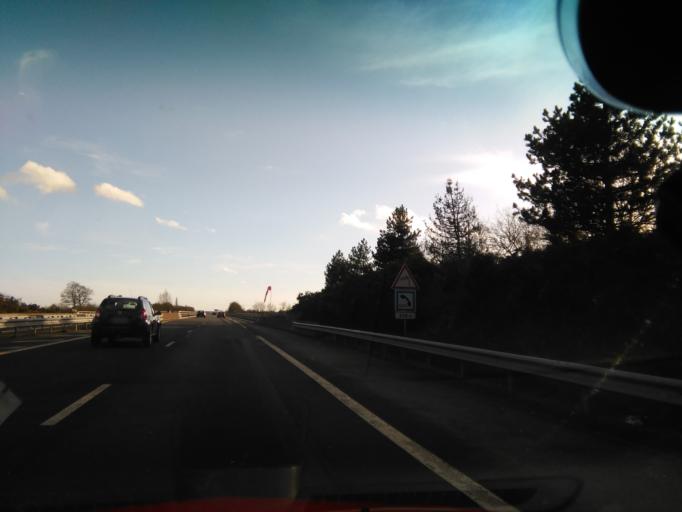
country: FR
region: Lower Normandy
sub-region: Departement du Calvados
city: Falaise
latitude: 48.8956
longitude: -0.2174
